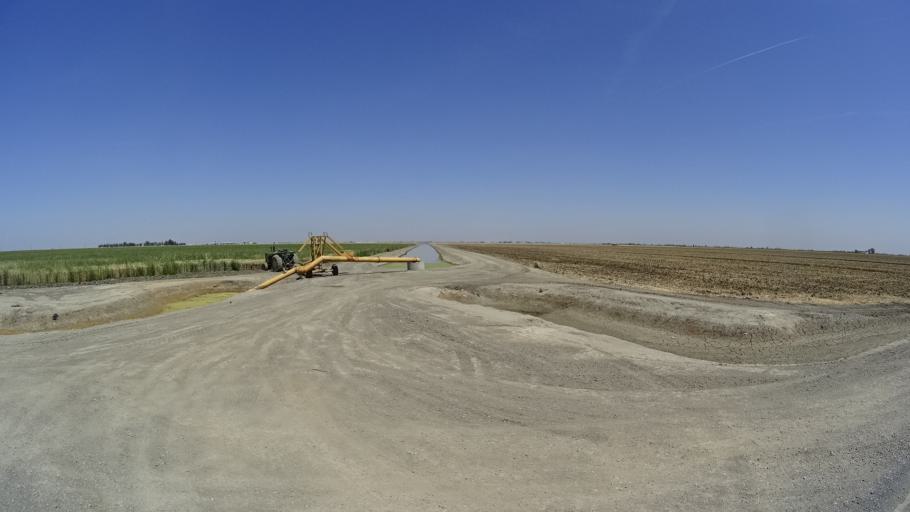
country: US
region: California
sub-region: Kings County
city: Corcoran
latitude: 36.0216
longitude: -119.5629
